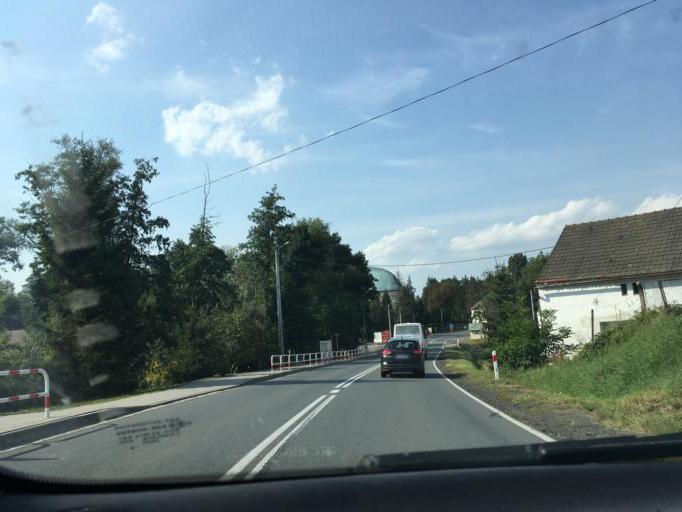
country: PL
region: Opole Voivodeship
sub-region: Powiat prudnicki
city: Laka Prudnicka
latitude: 50.3815
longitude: 17.5265
